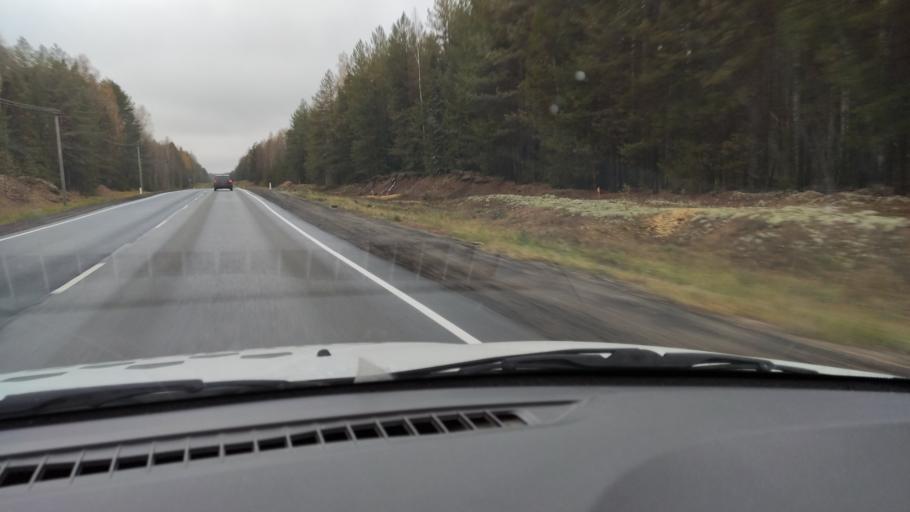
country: RU
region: Kirov
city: Belaya Kholunitsa
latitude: 58.9153
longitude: 51.1526
